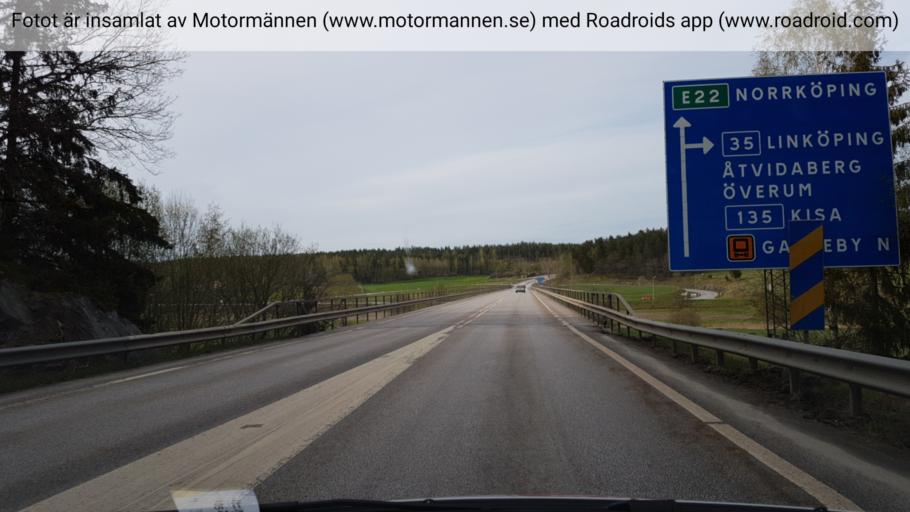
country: SE
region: Kalmar
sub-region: Vasterviks Kommun
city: Gamleby
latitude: 57.9048
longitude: 16.3836
